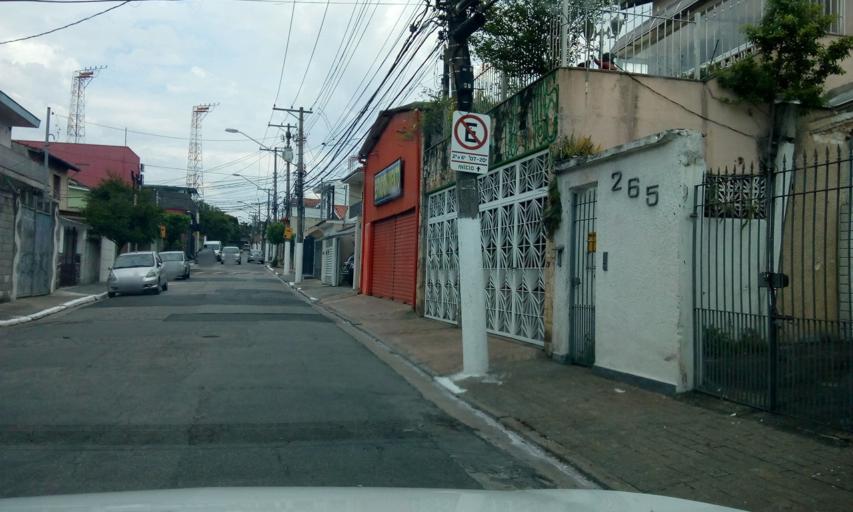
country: BR
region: Sao Paulo
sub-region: Sao Paulo
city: Sao Paulo
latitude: -23.6170
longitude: -46.6643
